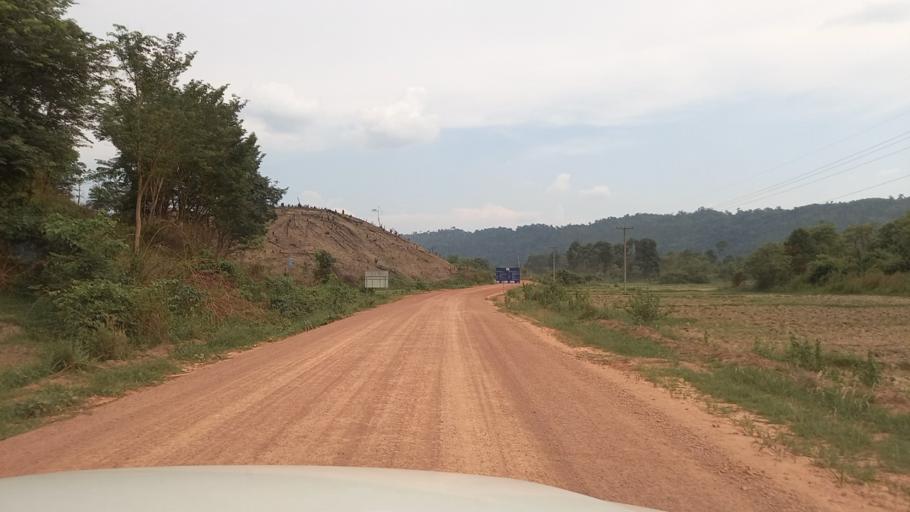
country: LA
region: Bolikhamxai
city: Bolikhan
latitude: 18.5090
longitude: 103.8433
